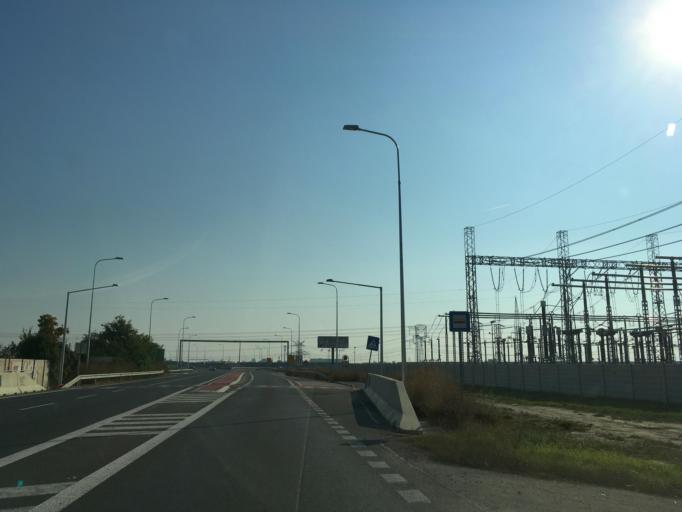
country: SK
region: Bratislavsky
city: Dunajska Luzna
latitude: 48.1130
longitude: 17.2197
